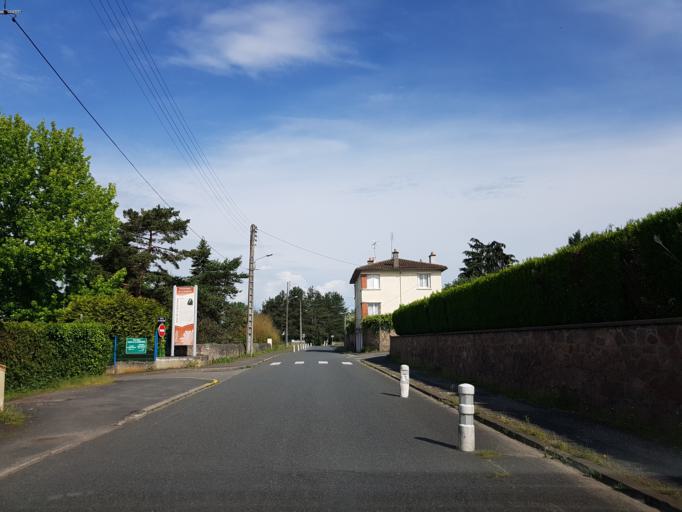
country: FR
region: Poitou-Charentes
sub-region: Departement de la Charente
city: Chabanais
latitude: 45.8772
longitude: 0.7164
